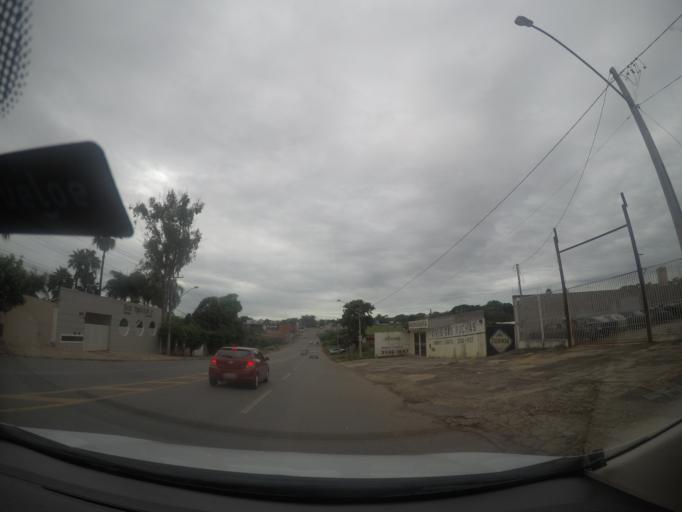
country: BR
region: Goias
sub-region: Goiania
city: Goiania
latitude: -16.6321
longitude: -49.2847
